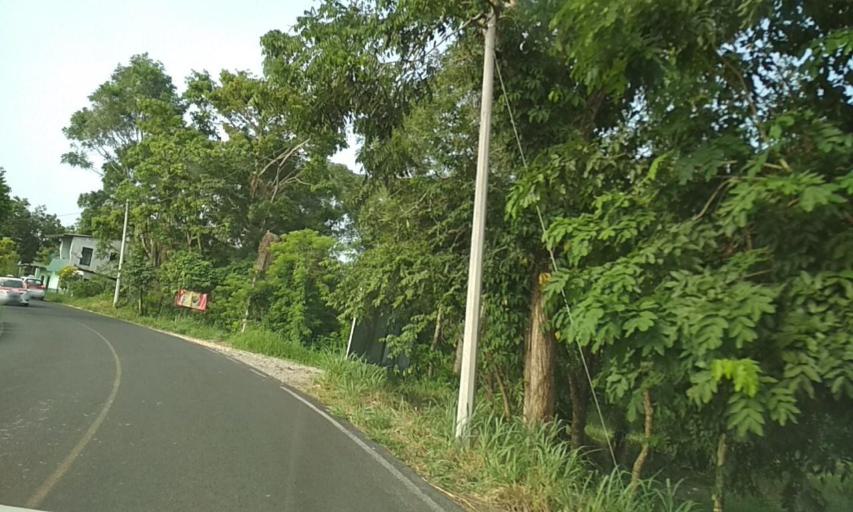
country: MX
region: Veracruz
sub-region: Misantla
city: La Defensa
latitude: 20.0535
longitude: -96.9784
